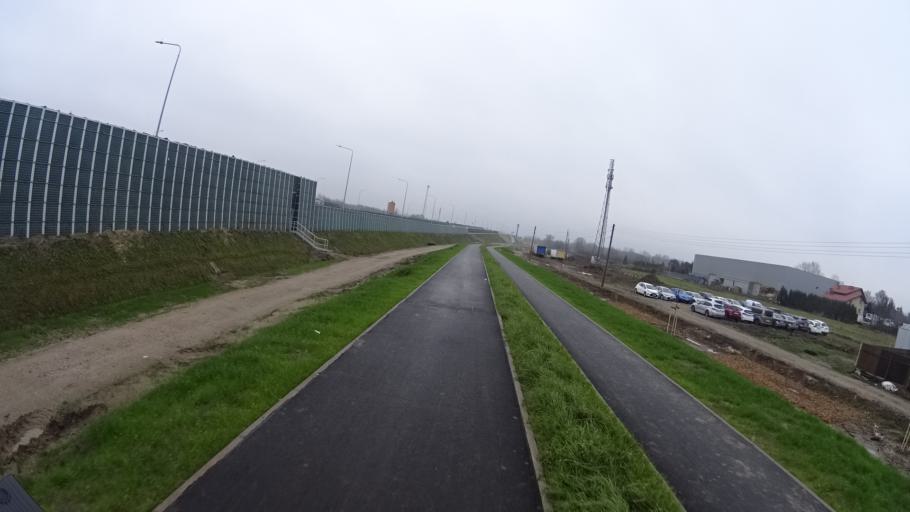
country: PL
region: Masovian Voivodeship
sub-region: Warszawa
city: Wilanow
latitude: 52.1573
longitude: 21.1251
